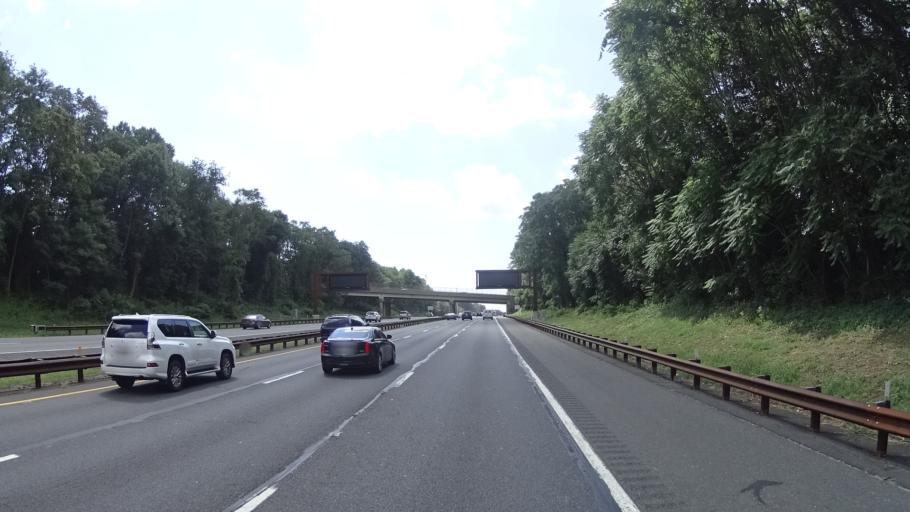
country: US
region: New Jersey
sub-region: Monmouth County
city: Tinton Falls
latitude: 40.3119
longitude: -74.0966
